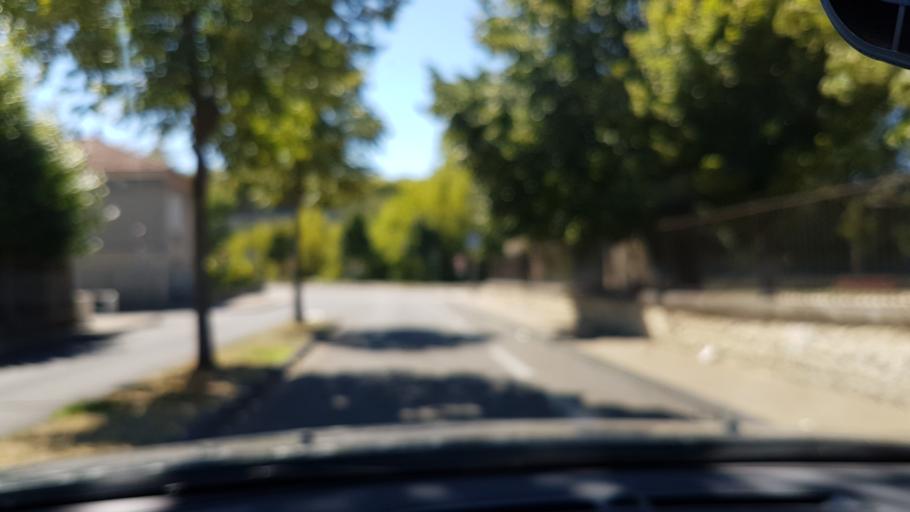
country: FR
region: Provence-Alpes-Cote d'Azur
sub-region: Departement du Vaucluse
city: Carpentras
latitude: 44.0584
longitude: 5.0451
